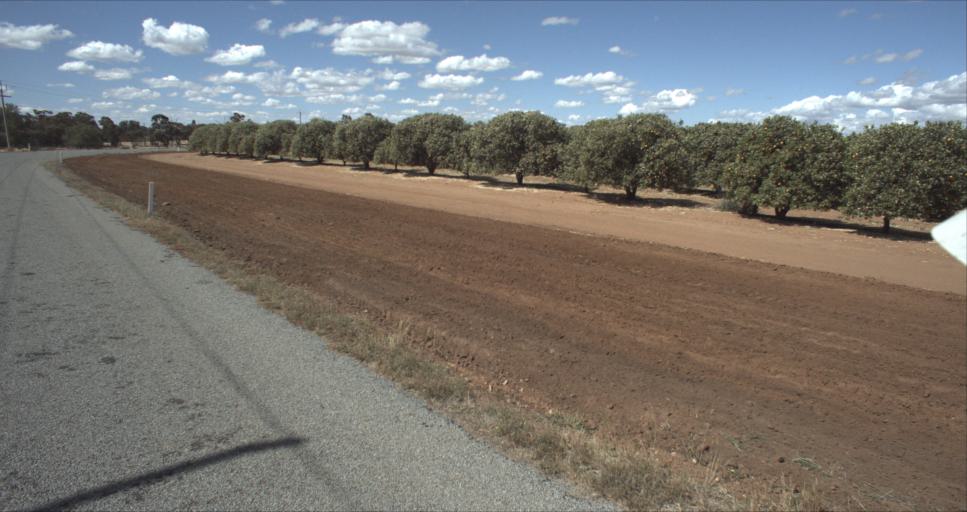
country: AU
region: New South Wales
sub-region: Leeton
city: Leeton
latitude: -34.5192
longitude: 146.2250
